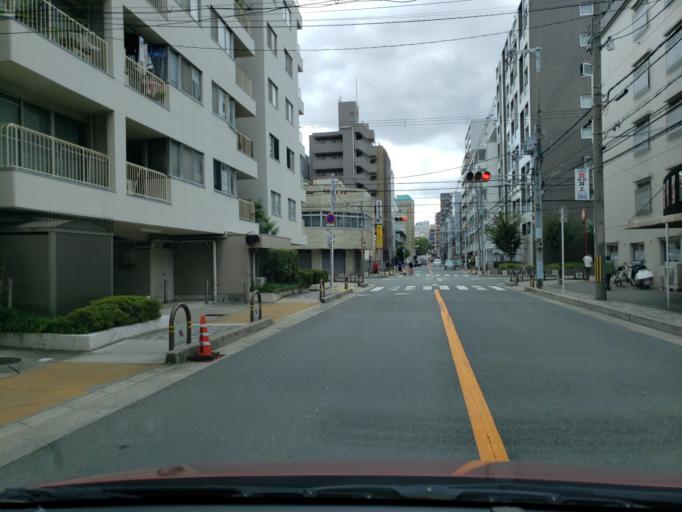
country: JP
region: Osaka
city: Suita
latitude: 34.7601
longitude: 135.5021
